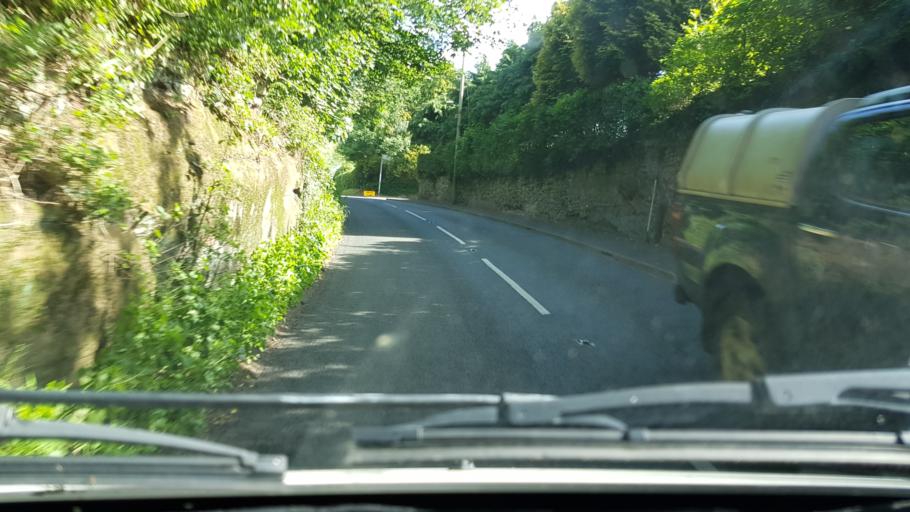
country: GB
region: England
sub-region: Worcestershire
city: Bewdley
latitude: 52.3698
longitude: -2.3125
